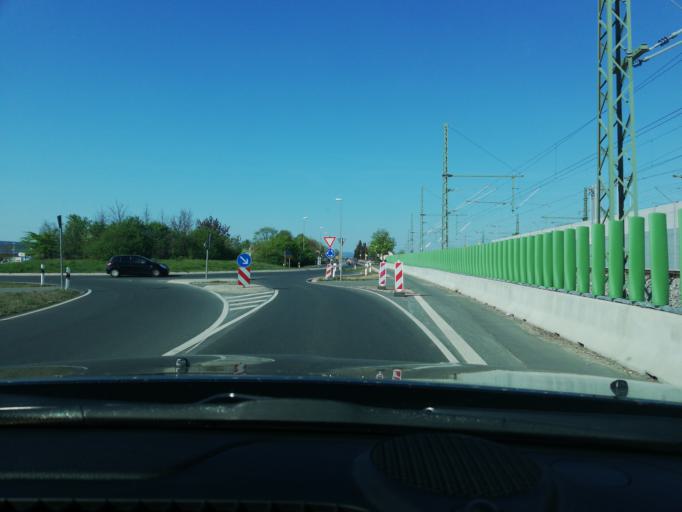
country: DE
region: Bavaria
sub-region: Regierungsbezirk Mittelfranken
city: Bubenreuth
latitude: 49.6280
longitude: 11.0103
